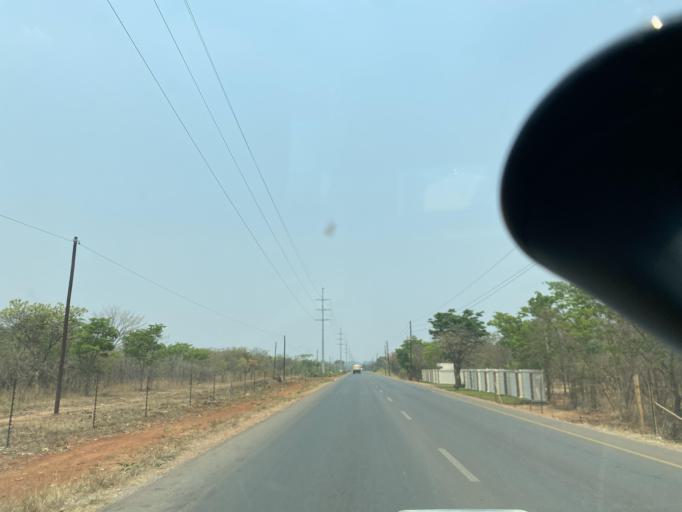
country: ZM
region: Lusaka
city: Lusaka
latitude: -15.5113
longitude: 28.4498
